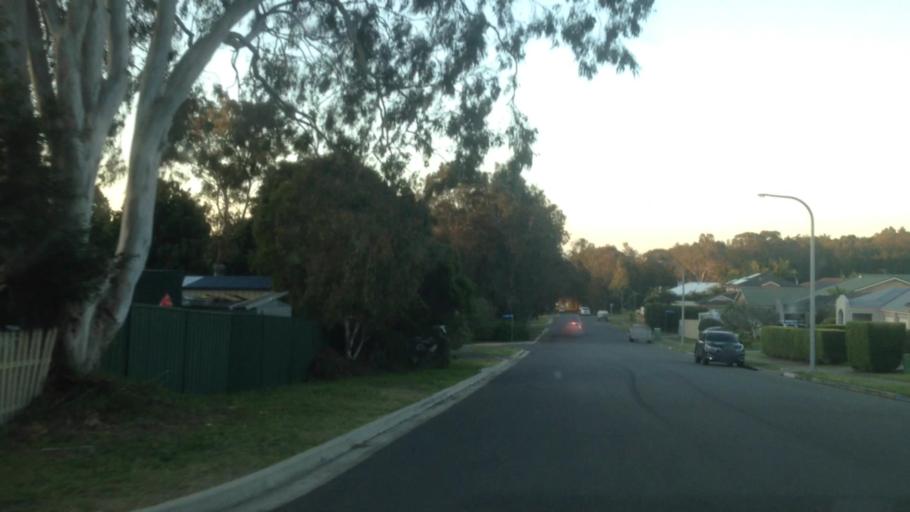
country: AU
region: New South Wales
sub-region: Wyong Shire
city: Kingfisher Shores
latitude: -33.1443
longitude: 151.5204
